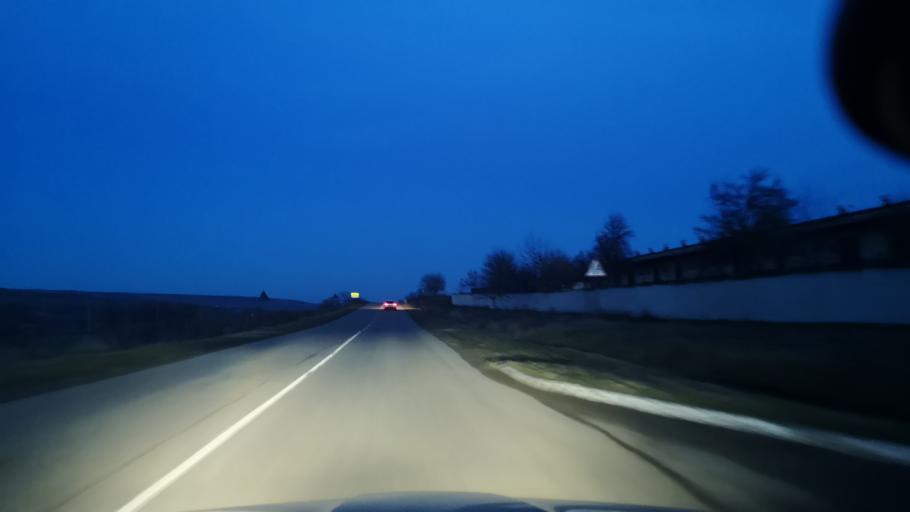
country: MD
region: Orhei
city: Orhei
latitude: 47.3399
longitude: 28.6584
